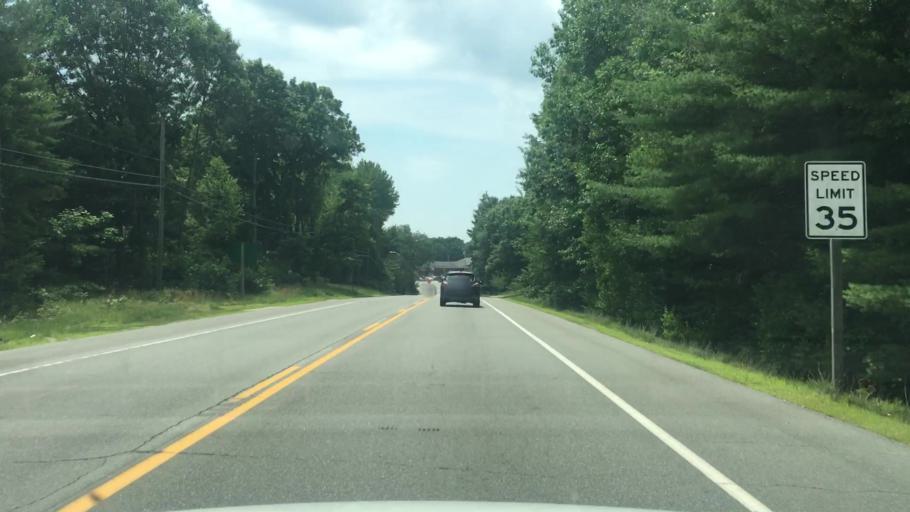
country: US
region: New Hampshire
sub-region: Strafford County
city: Rochester
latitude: 43.3394
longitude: -70.9383
